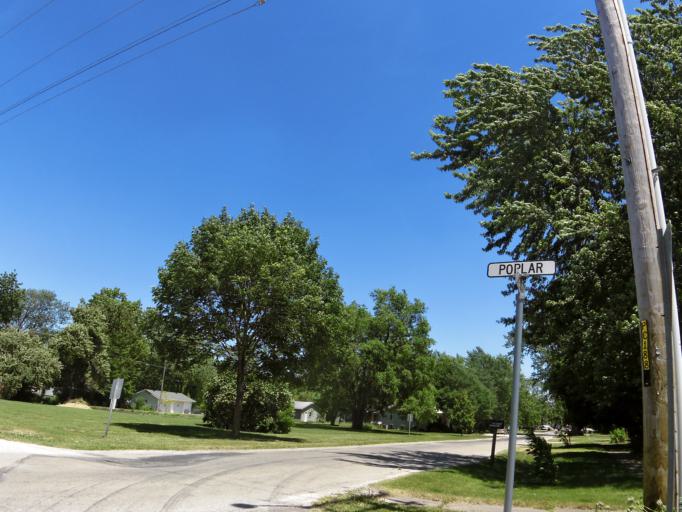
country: US
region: Illinois
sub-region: Livingston County
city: Chatsworth
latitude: 40.7541
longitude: -88.1864
